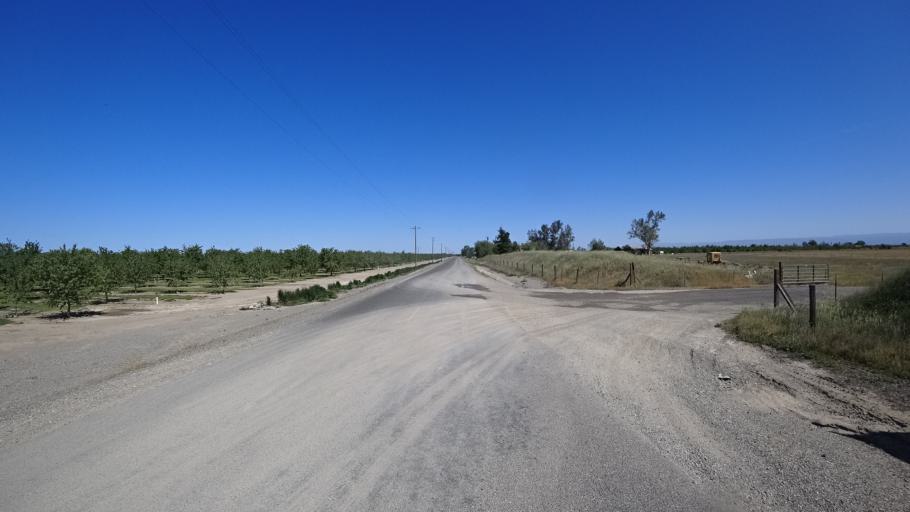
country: US
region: California
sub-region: Glenn County
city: Hamilton City
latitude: 39.6870
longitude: -122.1032
